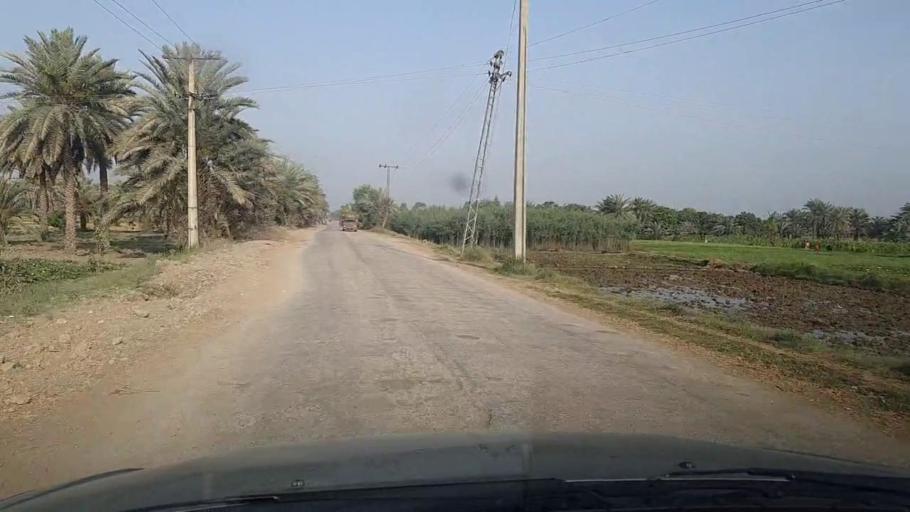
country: PK
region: Sindh
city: Pir jo Goth
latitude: 27.5710
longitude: 68.6028
